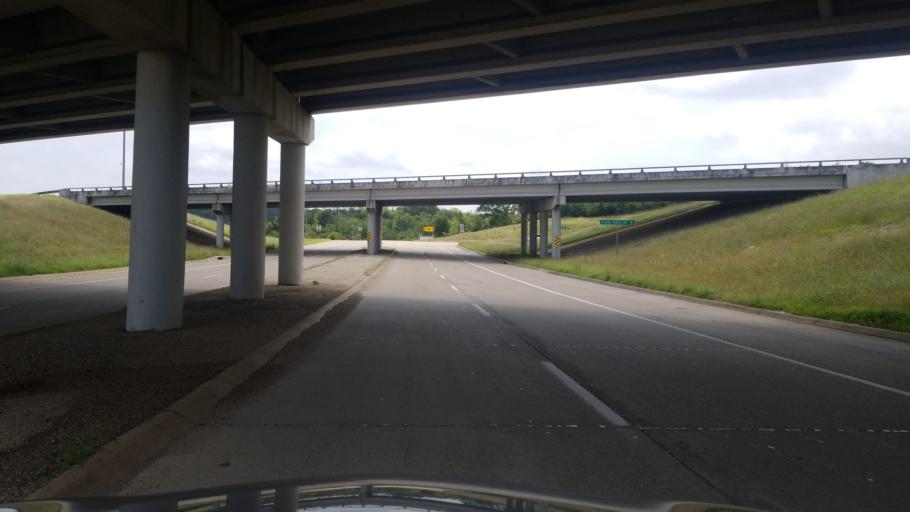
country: US
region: Texas
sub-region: Dallas County
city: Duncanville
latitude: 32.6910
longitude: -96.9392
